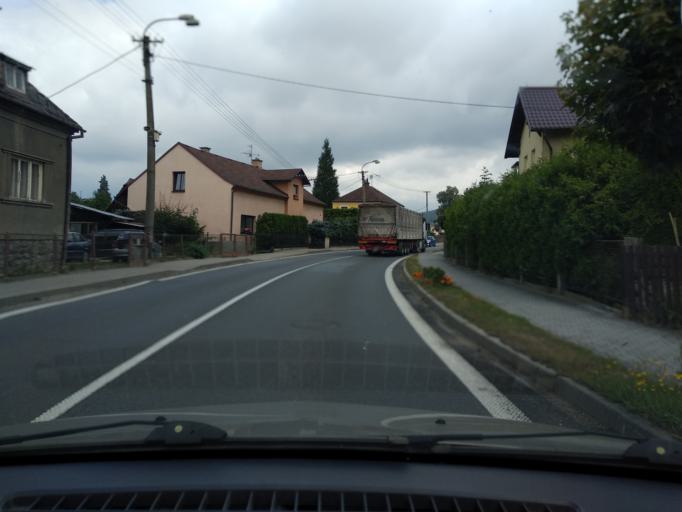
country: CZ
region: Olomoucky
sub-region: Okres Sumperk
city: Bludov
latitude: 49.9382
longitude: 16.9284
